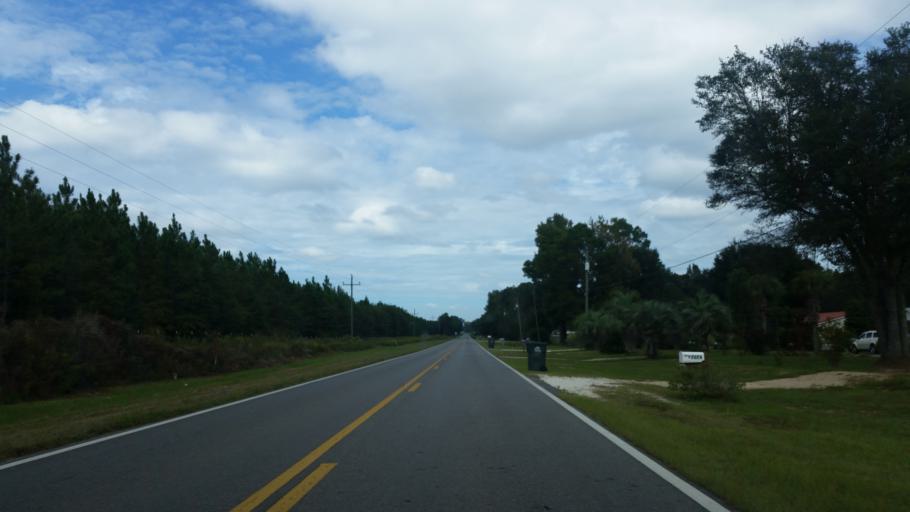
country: US
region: Florida
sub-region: Santa Rosa County
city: Point Baker
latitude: 30.6908
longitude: -86.9934
